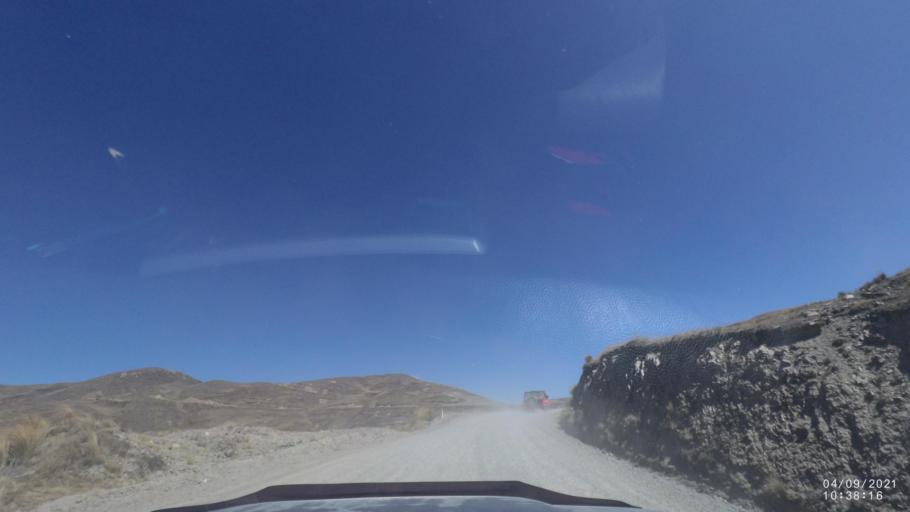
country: BO
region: Cochabamba
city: Sipe Sipe
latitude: -17.2875
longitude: -66.4569
